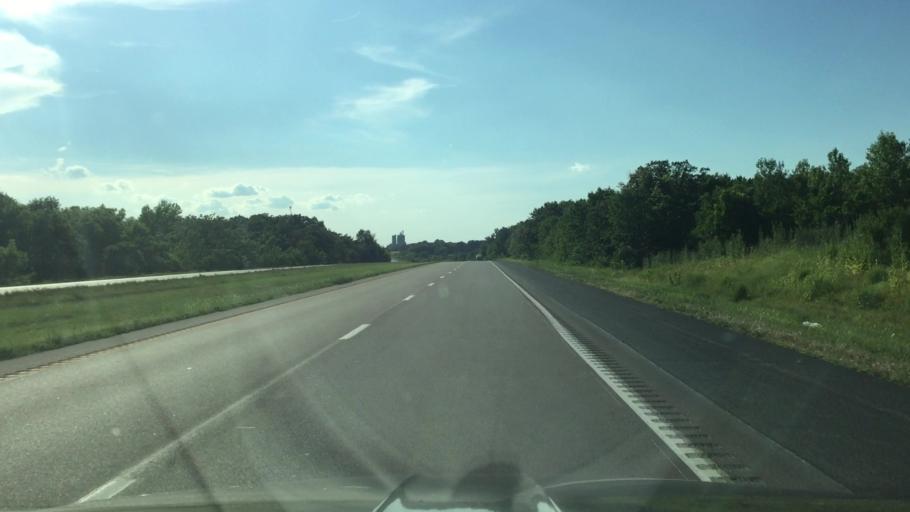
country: US
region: Missouri
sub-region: Pettis County
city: Sedalia
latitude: 38.7379
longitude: -93.3167
